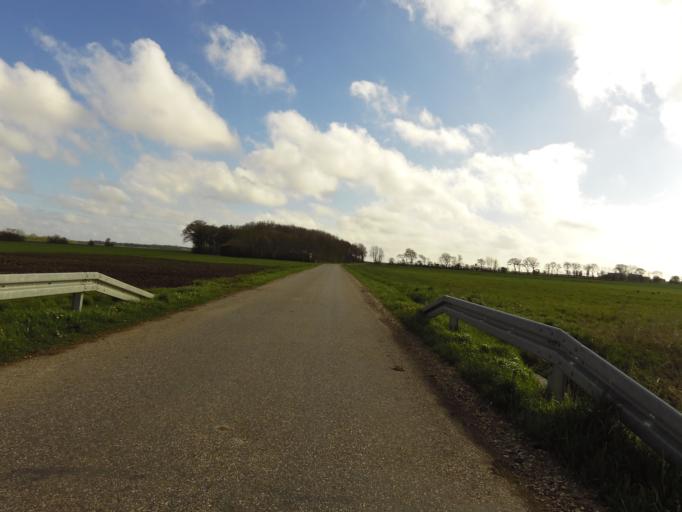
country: DK
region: South Denmark
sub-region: Vejen Kommune
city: Rodding
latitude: 55.3462
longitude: 8.9900
